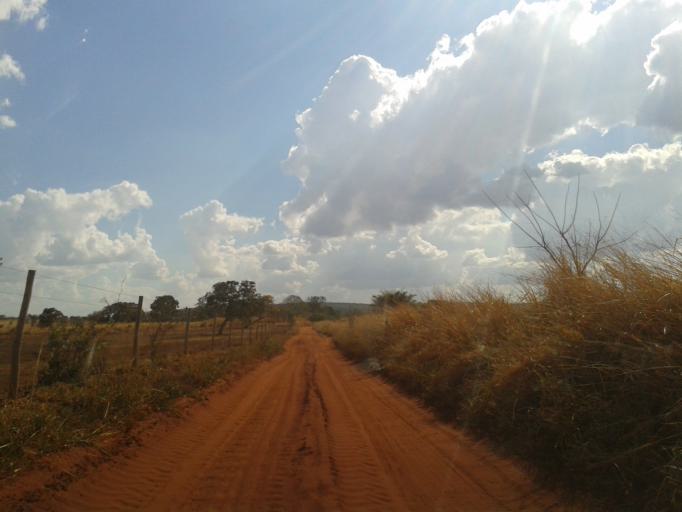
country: BR
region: Minas Gerais
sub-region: Santa Vitoria
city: Santa Vitoria
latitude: -19.2744
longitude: -50.0020
